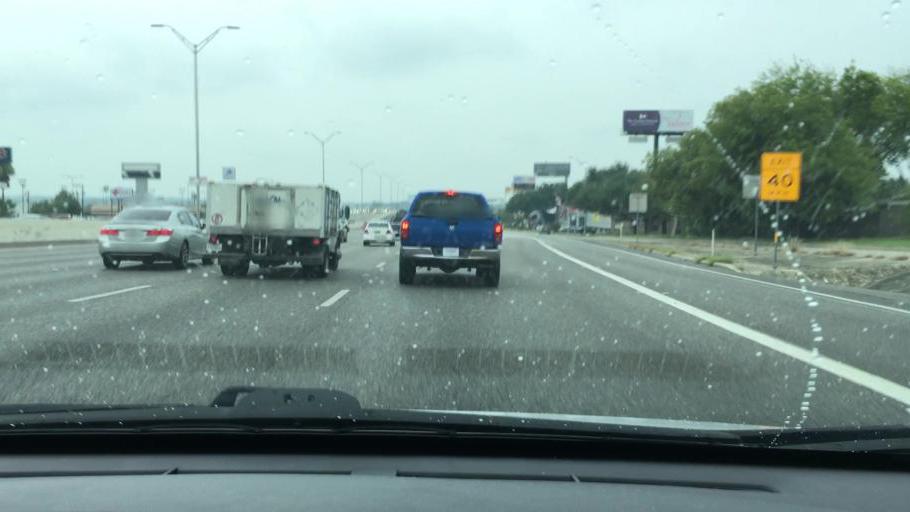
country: US
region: Texas
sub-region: Bexar County
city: Balcones Heights
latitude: 29.5097
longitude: -98.5399
